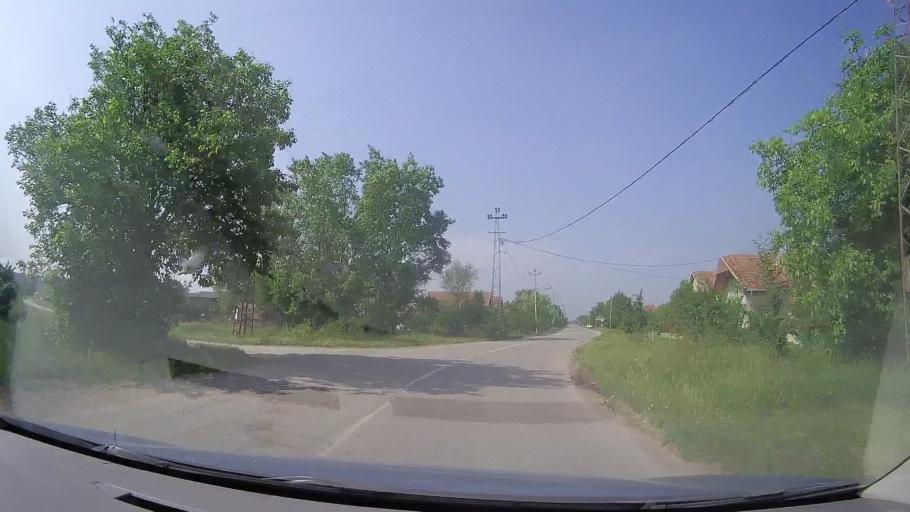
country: RS
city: Jasa Tomic
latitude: 45.4380
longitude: 20.8497
